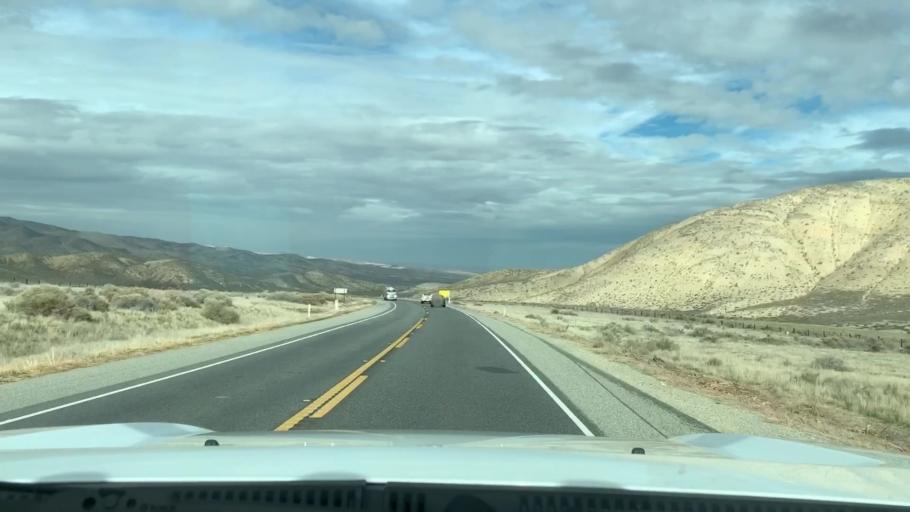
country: US
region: California
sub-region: Kern County
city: Maricopa
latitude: 35.0056
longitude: -119.4093
